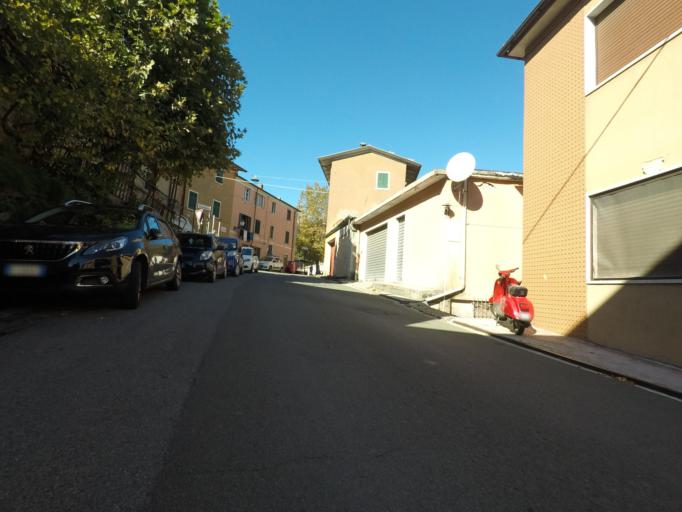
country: IT
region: Liguria
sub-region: Provincia di La Spezia
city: Casano-Dogana-Isola
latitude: 44.1126
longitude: 10.0744
